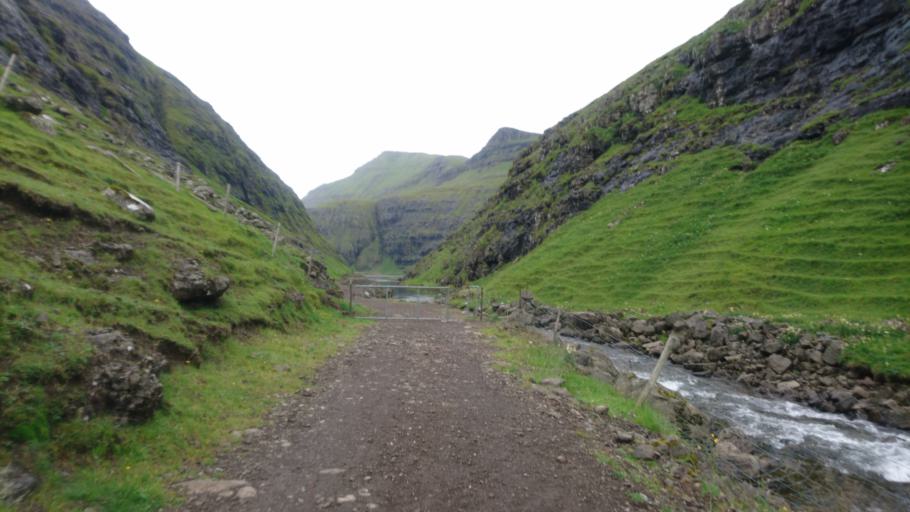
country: FO
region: Streymoy
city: Vestmanna
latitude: 62.2446
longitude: -7.1794
